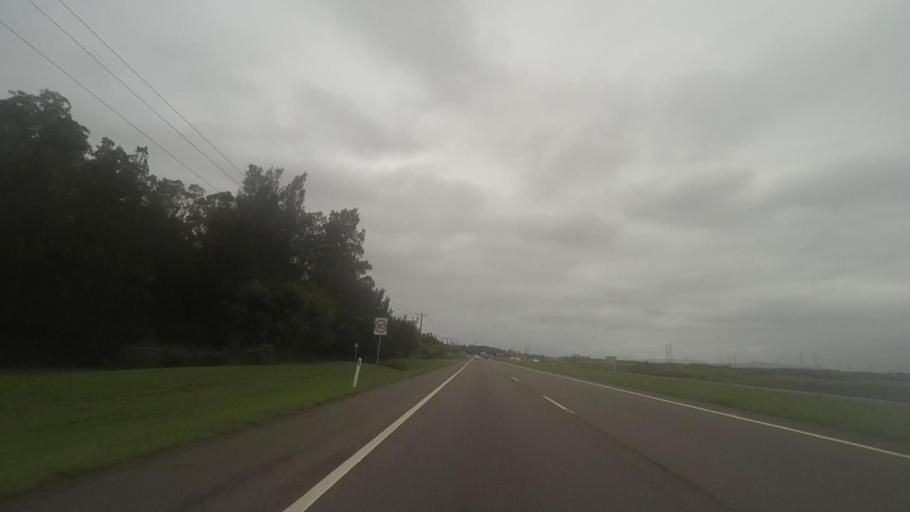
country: AU
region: New South Wales
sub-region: Port Stephens Shire
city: Raymond Terrace
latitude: -32.8021
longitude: 151.7150
